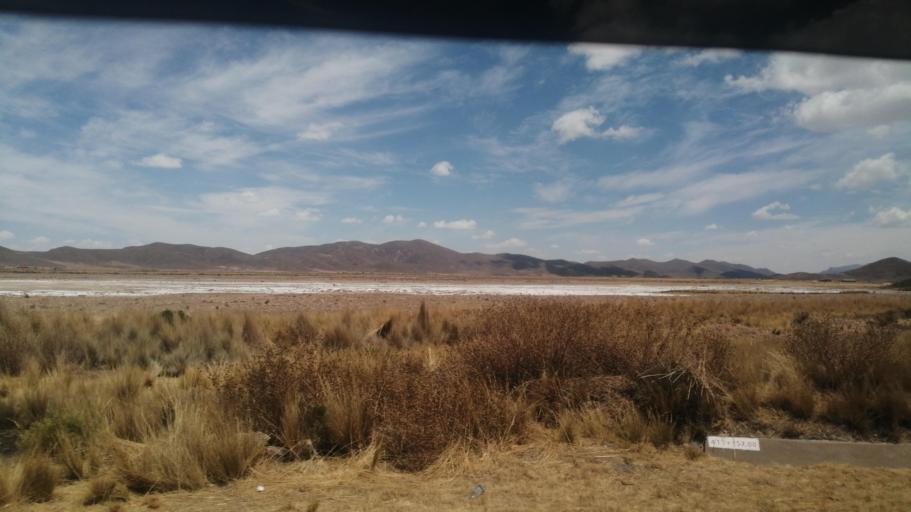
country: BO
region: Oruro
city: Challapata
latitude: -18.7255
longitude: -66.8668
